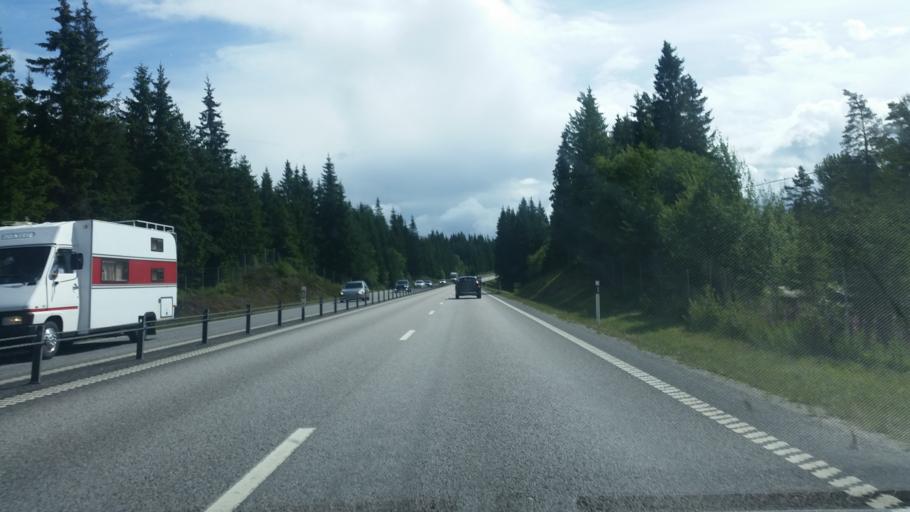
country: SE
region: Joenkoeping
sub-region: Mullsjo Kommun
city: Mullsjoe
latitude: 57.7731
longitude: 13.7024
